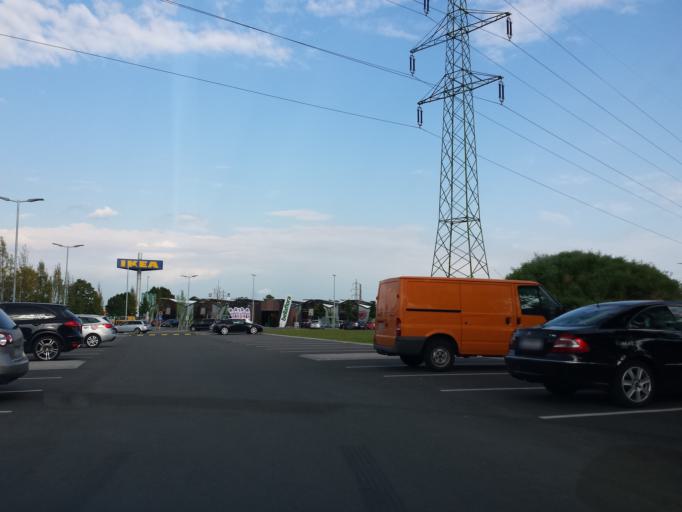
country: AT
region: Styria
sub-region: Graz Stadt
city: Wetzelsdorf
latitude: 47.0314
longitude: 15.4206
